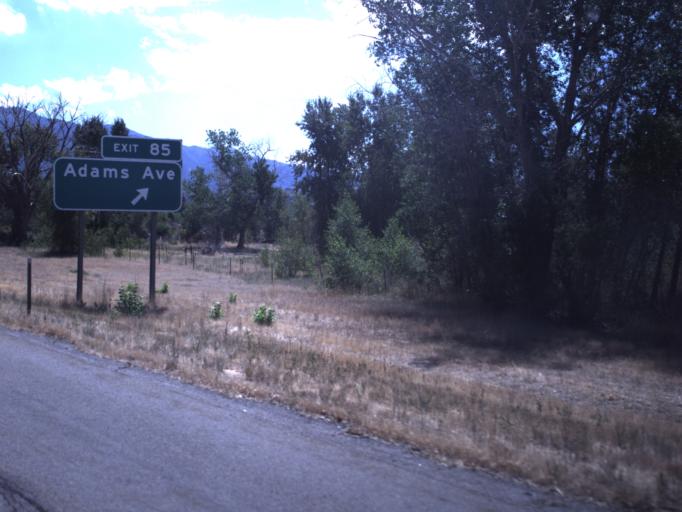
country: US
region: Utah
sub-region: Weber County
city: Washington Terrace
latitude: 41.1521
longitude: -111.9761
